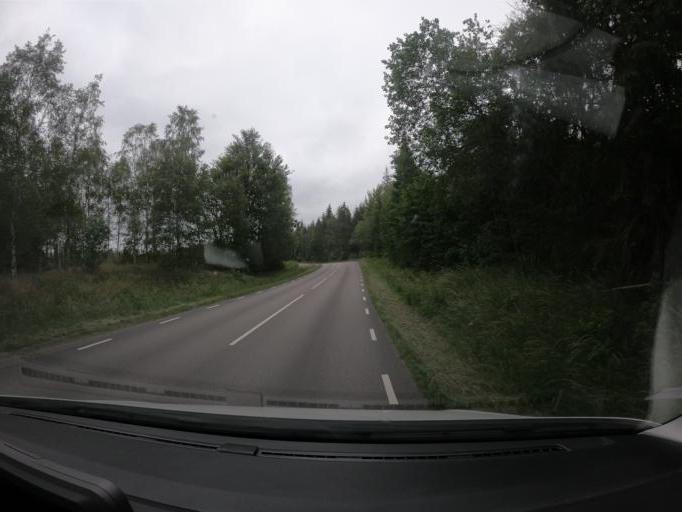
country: SE
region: Skane
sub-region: Perstorps Kommun
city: Perstorp
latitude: 56.0934
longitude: 13.4104
